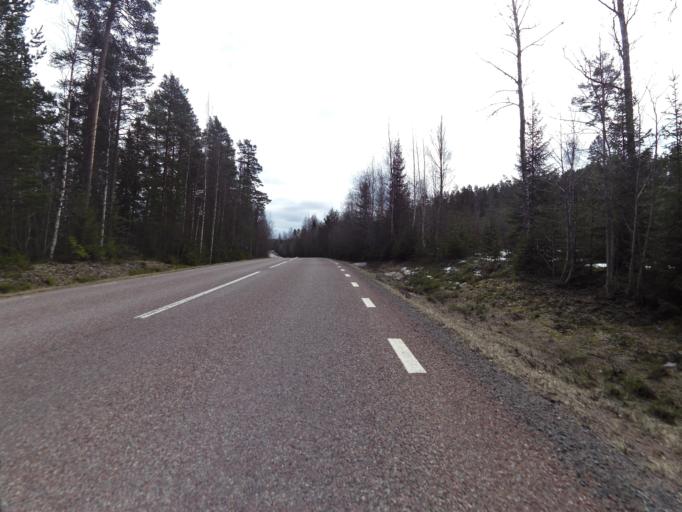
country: SE
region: Dalarna
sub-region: Hedemora Kommun
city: Langshyttan
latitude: 60.5430
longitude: 16.1240
